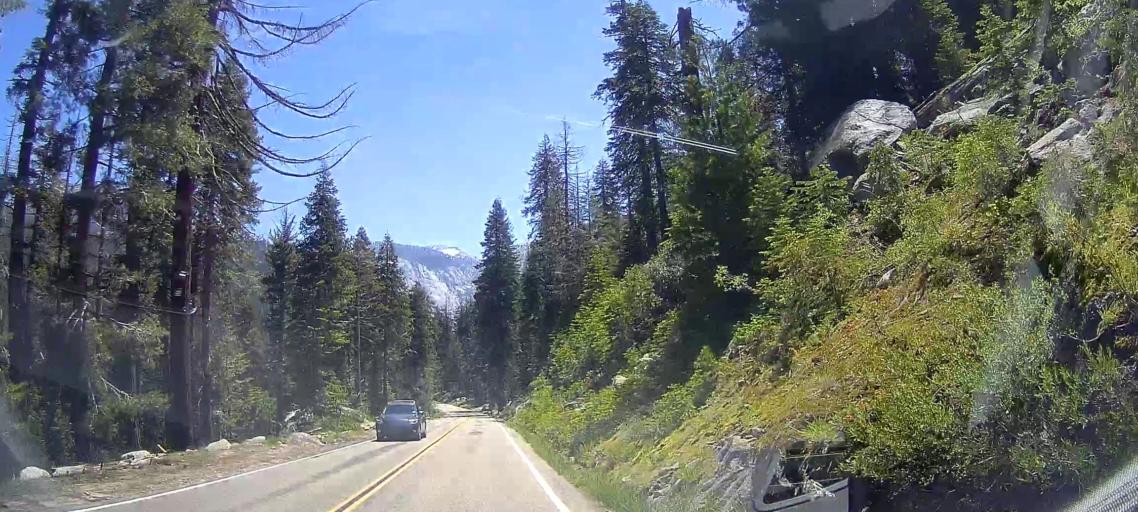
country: US
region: California
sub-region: Tulare County
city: Three Rivers
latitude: 36.6023
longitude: -118.7394
